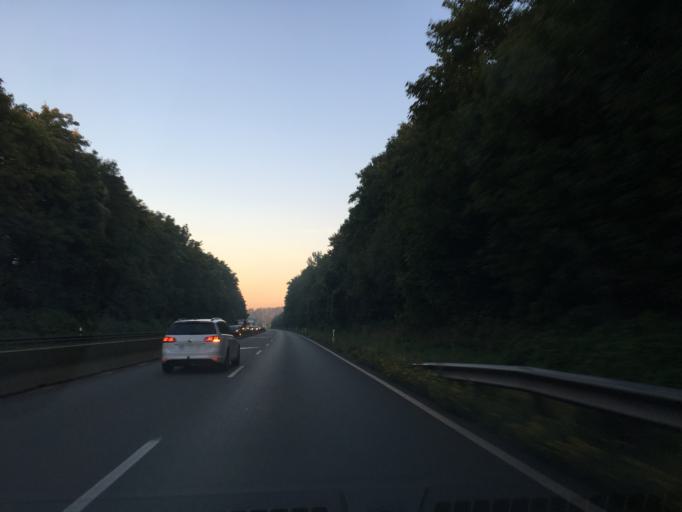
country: DE
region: North Rhine-Westphalia
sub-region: Regierungsbezirk Munster
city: Altenberge
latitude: 52.0314
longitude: 7.4803
